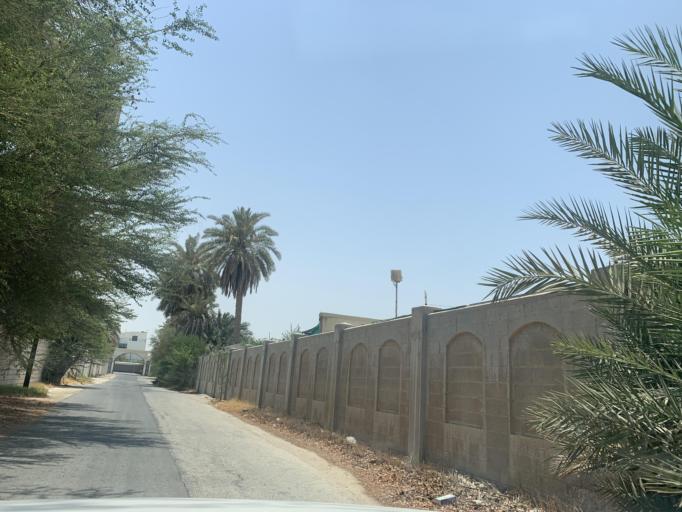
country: BH
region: Manama
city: Jidd Hafs
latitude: 26.2056
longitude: 50.4753
